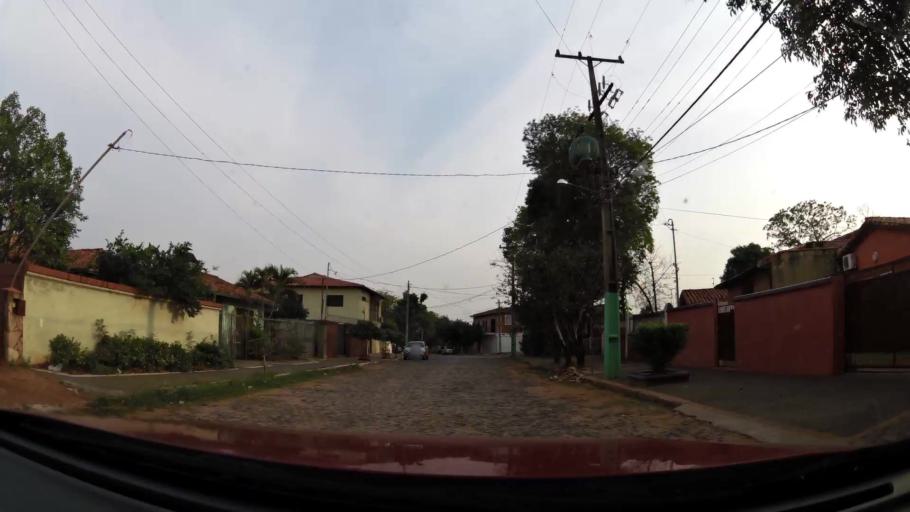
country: PY
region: Central
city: Lambare
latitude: -25.3304
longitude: -57.5768
